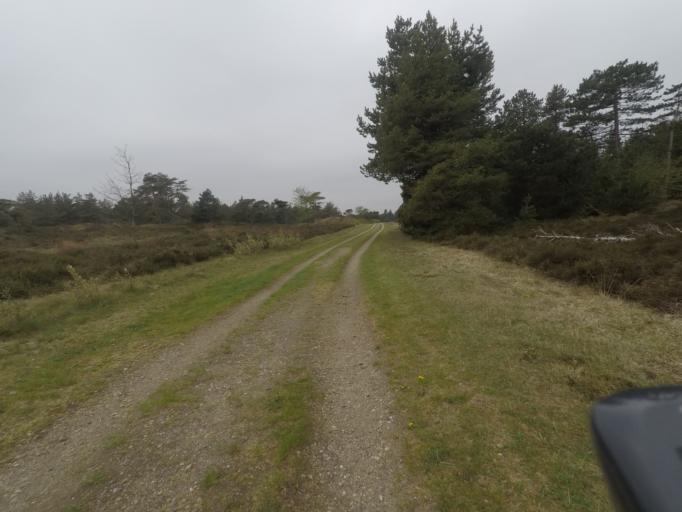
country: DE
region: Schleswig-Holstein
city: List
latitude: 55.1240
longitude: 8.5449
